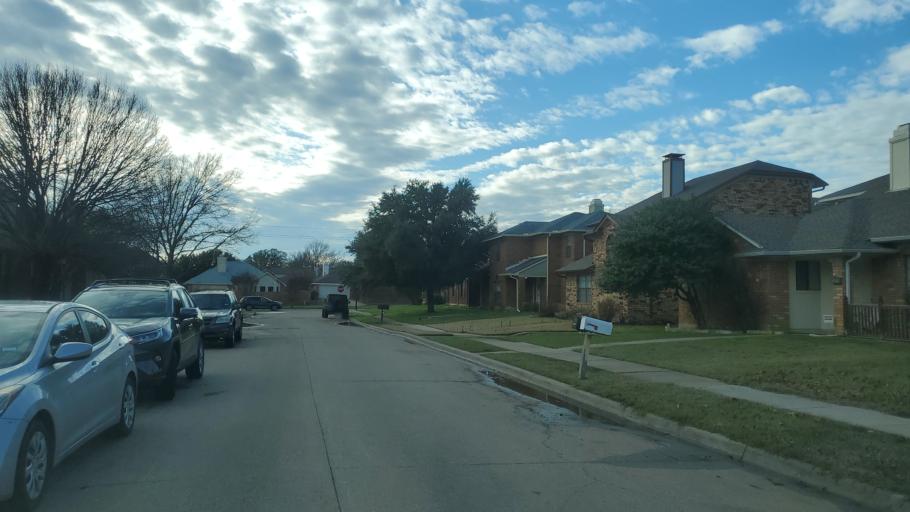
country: US
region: Texas
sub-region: Dallas County
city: Carrollton
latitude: 32.9967
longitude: -96.9015
